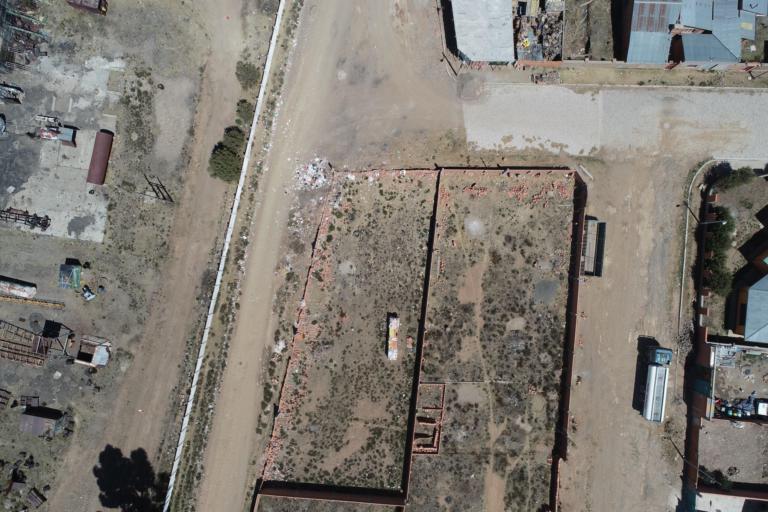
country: BO
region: La Paz
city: La Paz
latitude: -16.5671
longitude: -68.1925
